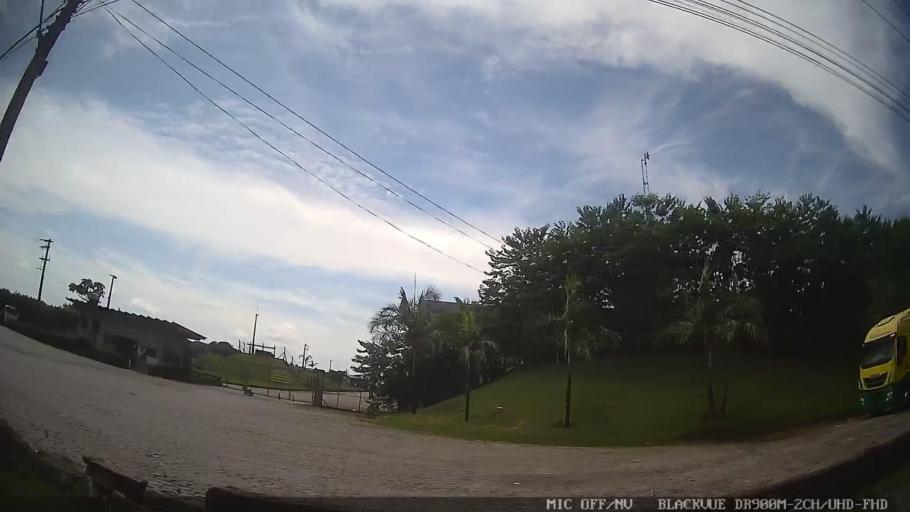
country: BR
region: Sao Paulo
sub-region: Aruja
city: Aruja
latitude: -23.4322
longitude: -46.2553
